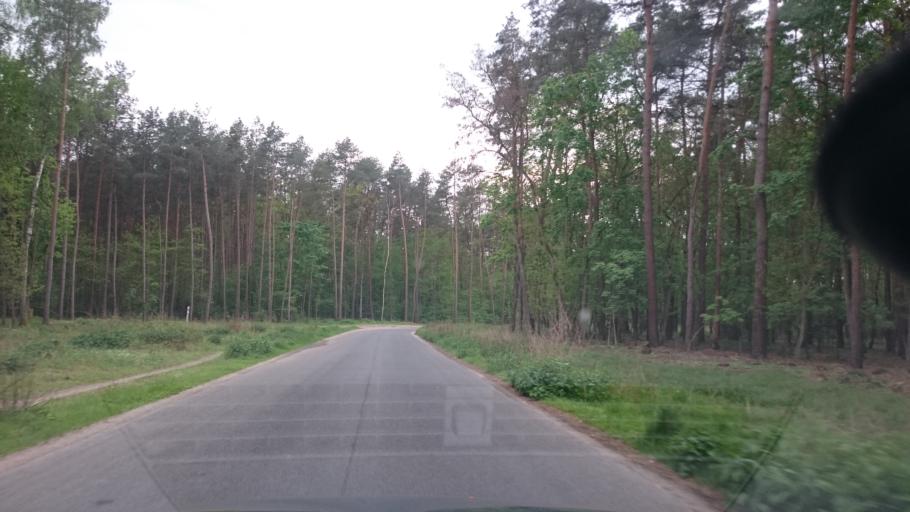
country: PL
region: Kujawsko-Pomorskie
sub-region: Grudziadz
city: Grudziadz
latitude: 53.4412
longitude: 18.7729
